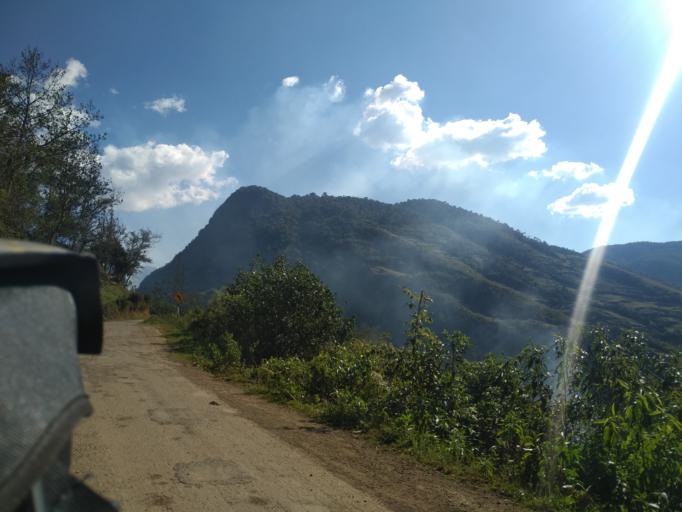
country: PE
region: Amazonas
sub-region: Provincia de Chachapoyas
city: Montevideo
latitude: -6.7157
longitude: -77.8199
